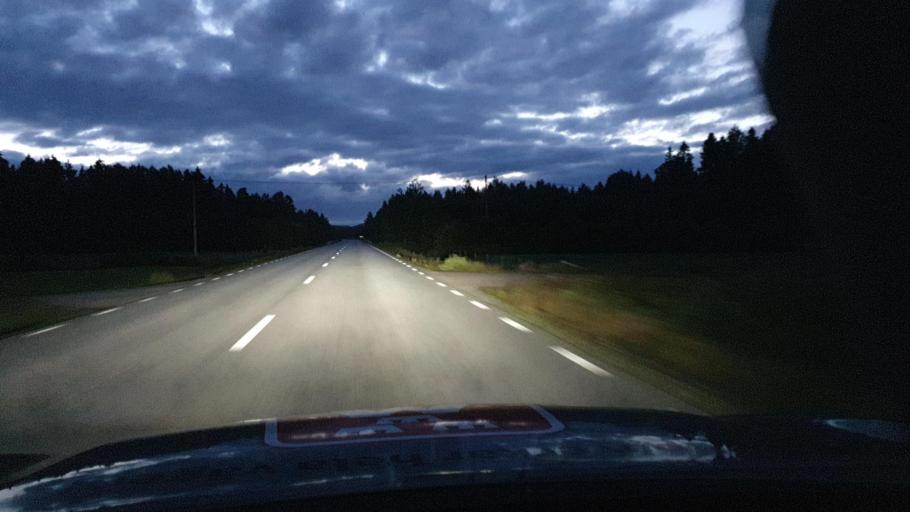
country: SE
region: OErebro
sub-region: Karlskoga Kommun
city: Karlskoga
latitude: 59.4245
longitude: 14.5155
